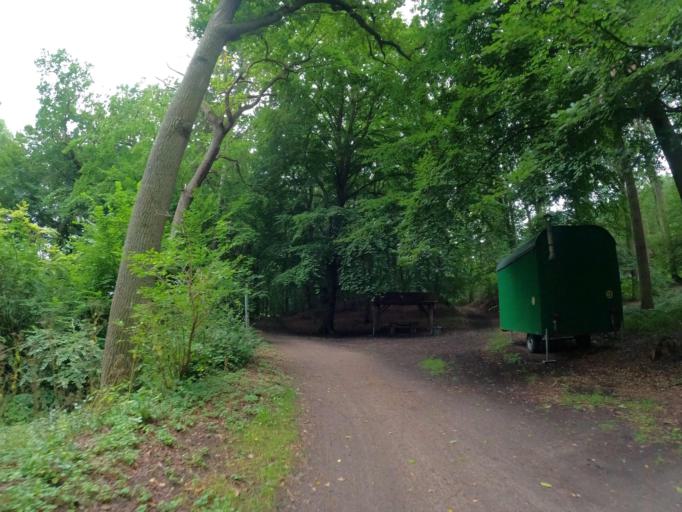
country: DE
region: Mecklenburg-Vorpommern
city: Ostseebad Binz
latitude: 54.3564
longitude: 13.5954
